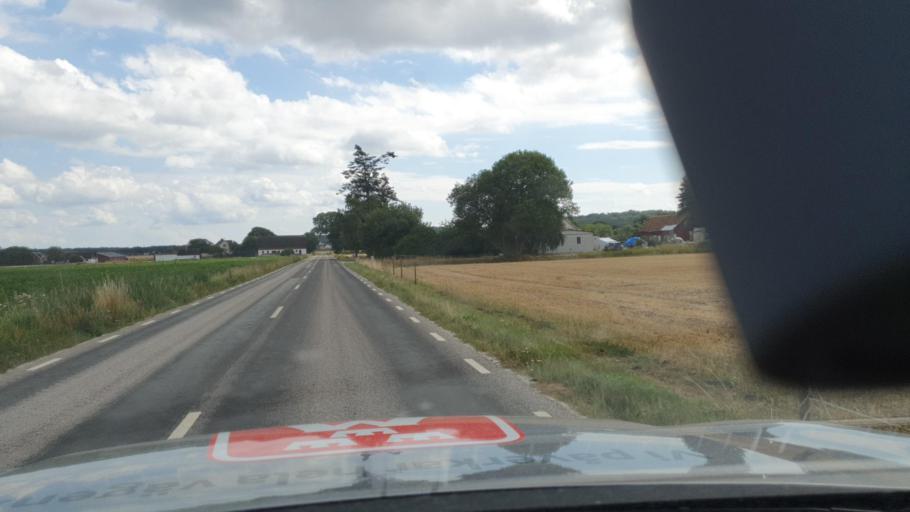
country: SE
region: Blekinge
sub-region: Solvesborgs Kommun
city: Soelvesborg
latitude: 56.0389
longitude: 14.7152
